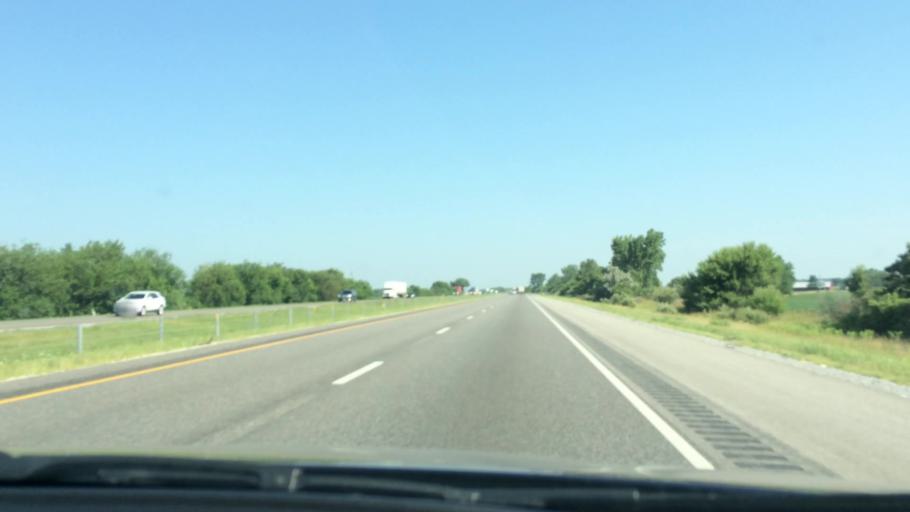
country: US
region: Indiana
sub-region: Jasper County
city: Remington
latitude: 40.7783
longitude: -87.1273
